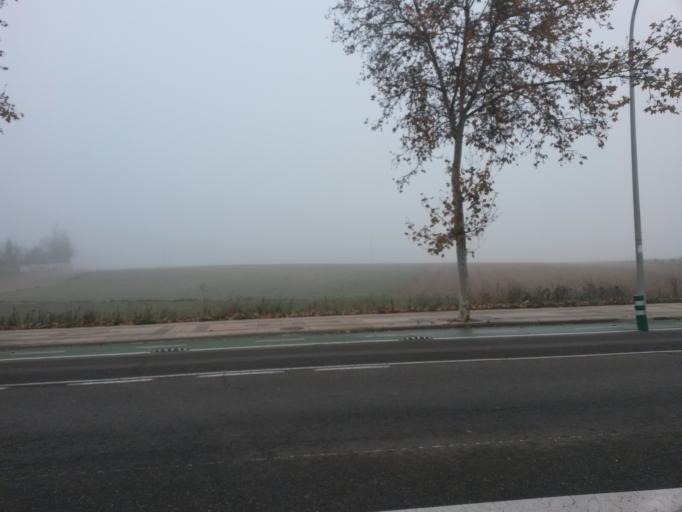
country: ES
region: Castille and Leon
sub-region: Provincia de Salamanca
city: Salamanca
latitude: 40.9825
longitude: -5.6536
